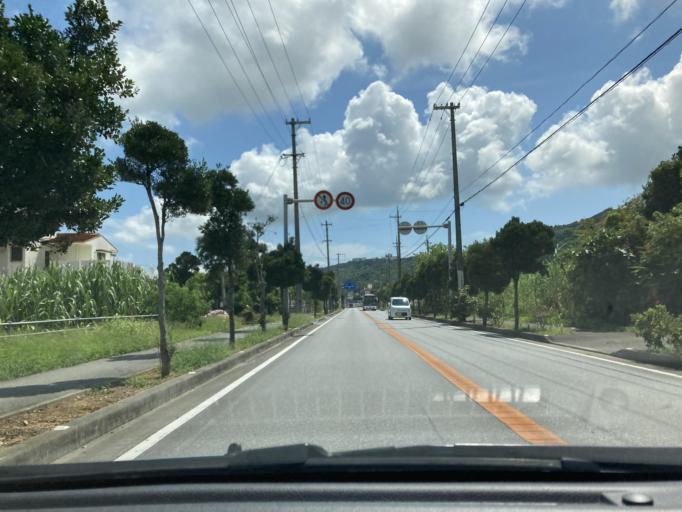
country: JP
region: Okinawa
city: Tomigusuku
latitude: 26.1725
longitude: 127.7703
